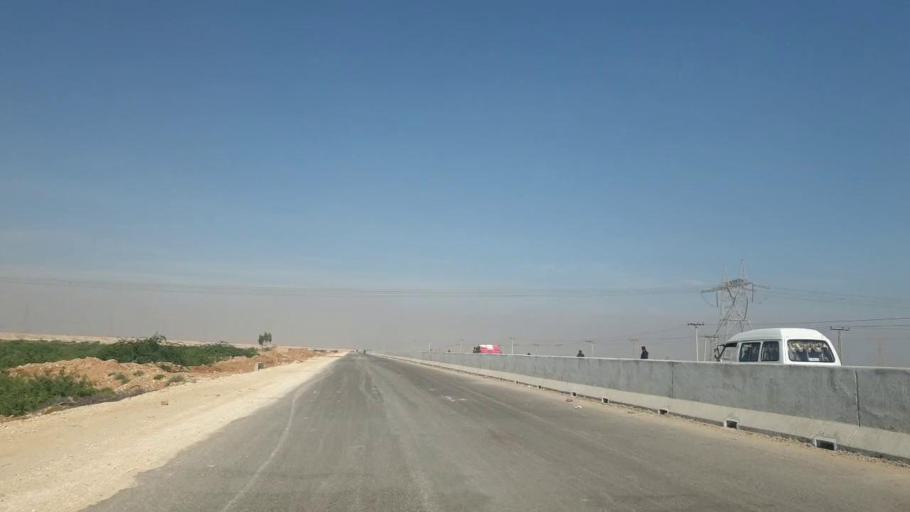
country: PK
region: Sindh
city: Jamshoro
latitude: 25.4835
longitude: 68.2720
